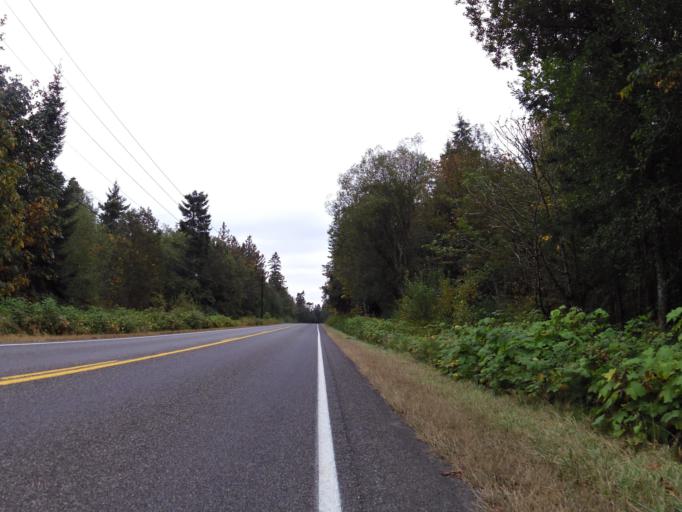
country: US
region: Washington
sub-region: Jefferson County
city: Port Ludlow
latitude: 47.9828
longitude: -122.7161
